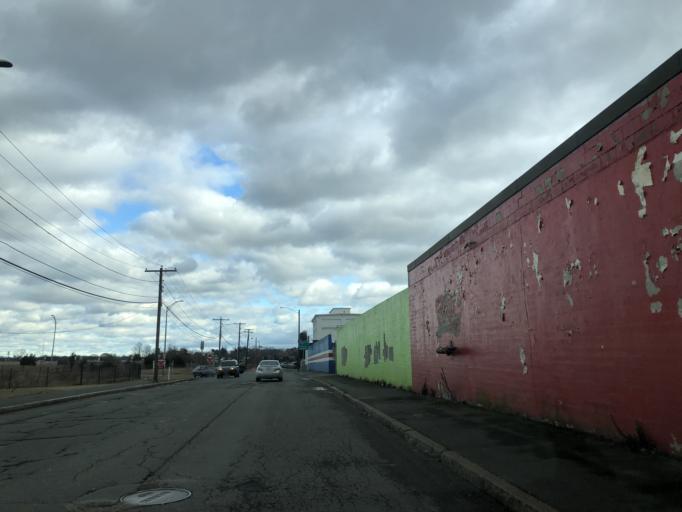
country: US
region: Massachusetts
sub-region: Bristol County
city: New Bedford
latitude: 41.6538
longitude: -70.9230
